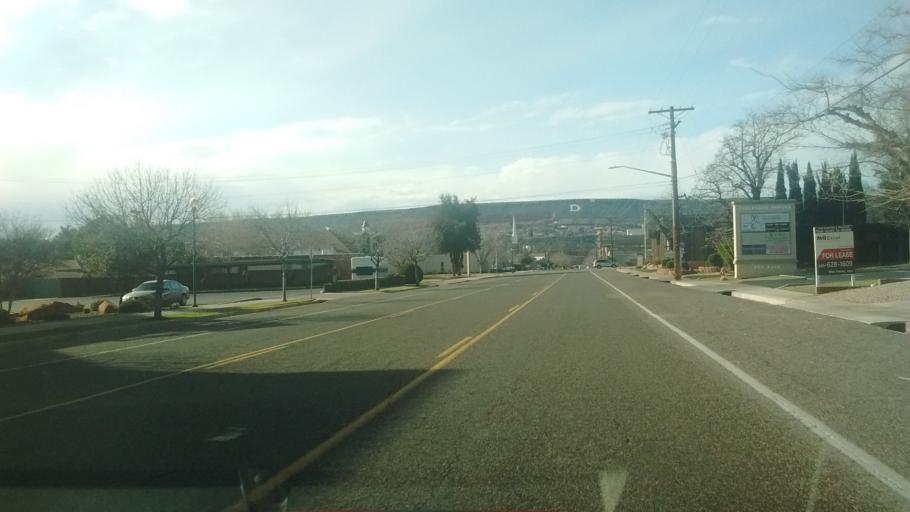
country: US
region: Utah
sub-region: Washington County
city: Saint George
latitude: 37.1082
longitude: -113.5774
